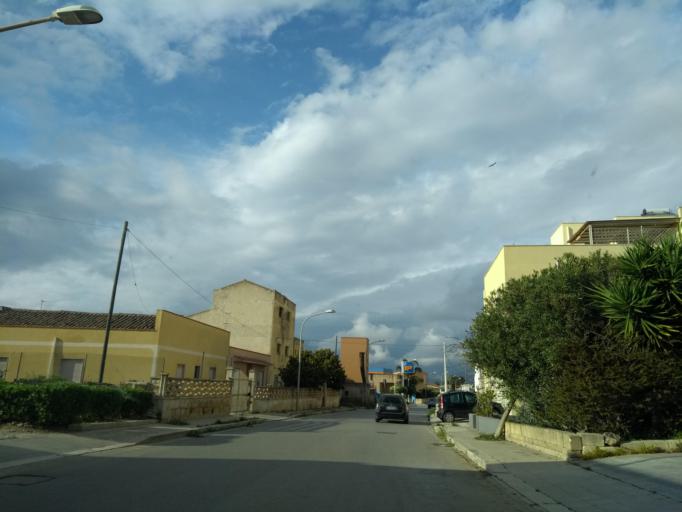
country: IT
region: Sicily
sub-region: Trapani
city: Marausa
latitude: 37.9424
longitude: 12.5106
